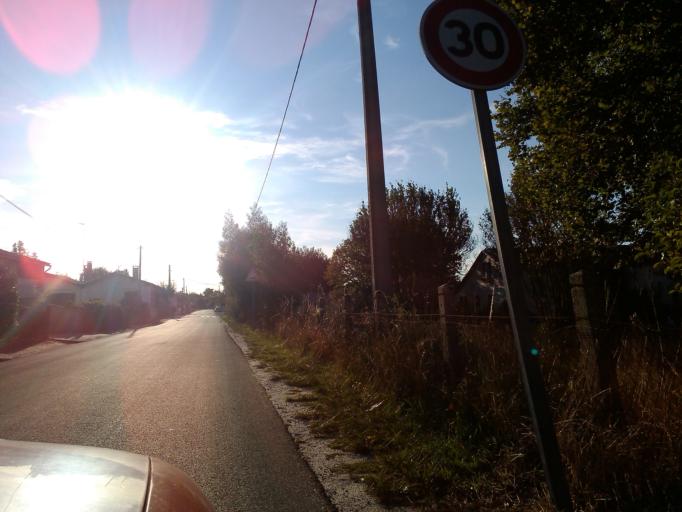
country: FR
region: Aquitaine
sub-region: Departement de la Gironde
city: Soulac-sur-Mer
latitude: 45.4315
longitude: -1.0368
